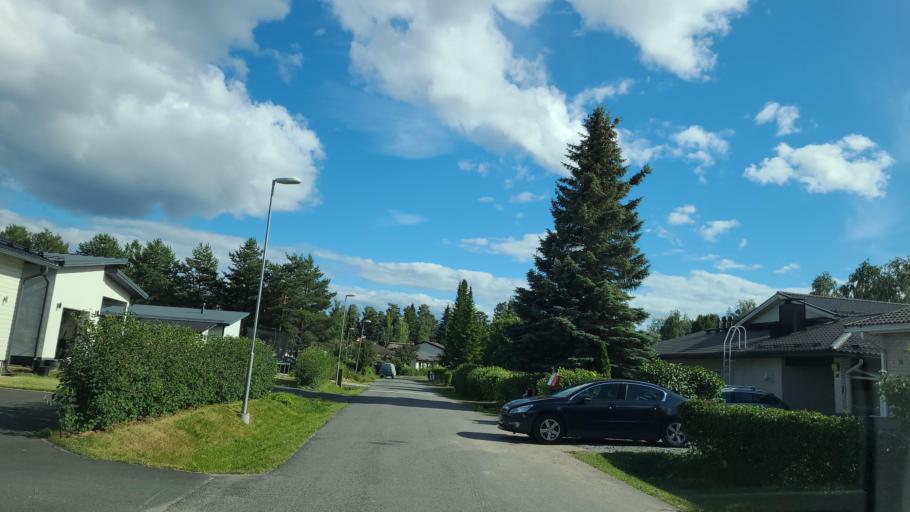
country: FI
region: Northern Savo
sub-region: Kuopio
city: Kuopio
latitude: 62.9279
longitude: 27.6282
